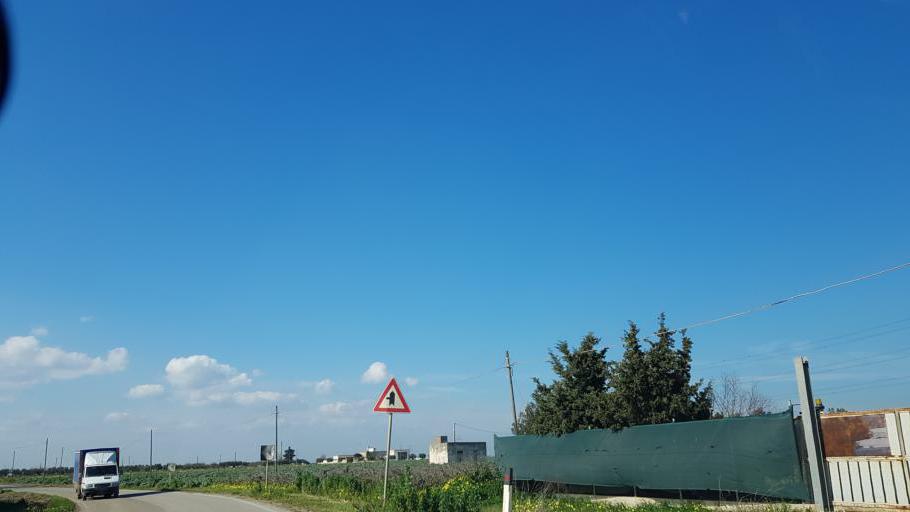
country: IT
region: Apulia
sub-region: Provincia di Brindisi
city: La Rosa
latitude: 40.5917
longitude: 17.9394
